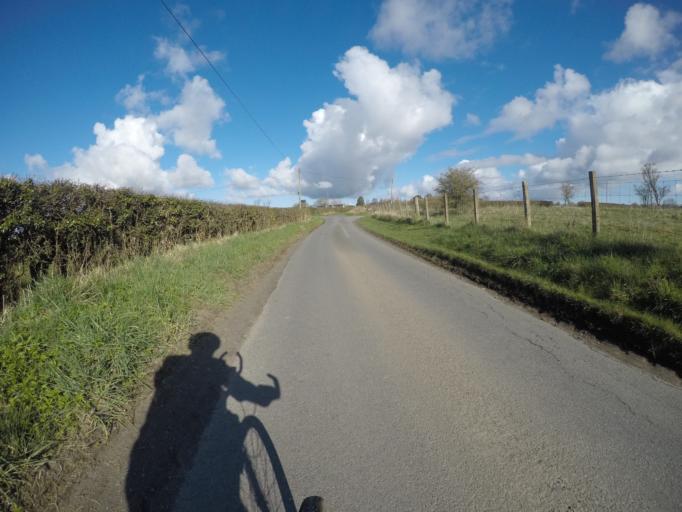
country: GB
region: Scotland
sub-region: North Ayrshire
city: Irvine
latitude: 55.6559
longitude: -4.6538
